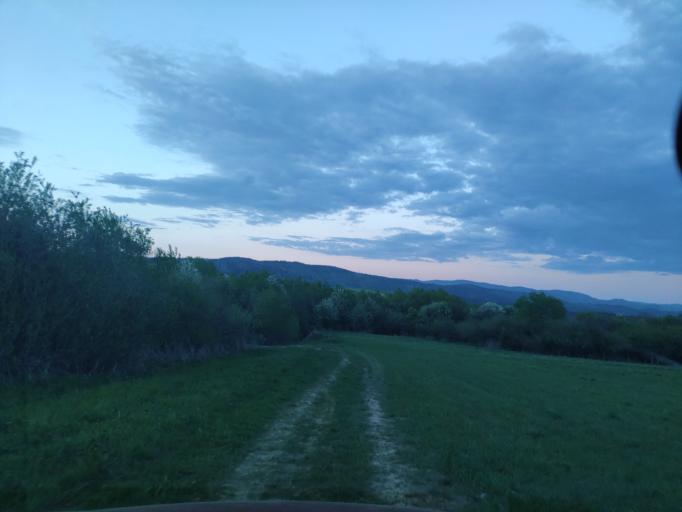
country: SK
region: Presovsky
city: Lipany
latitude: 49.1801
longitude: 20.8150
